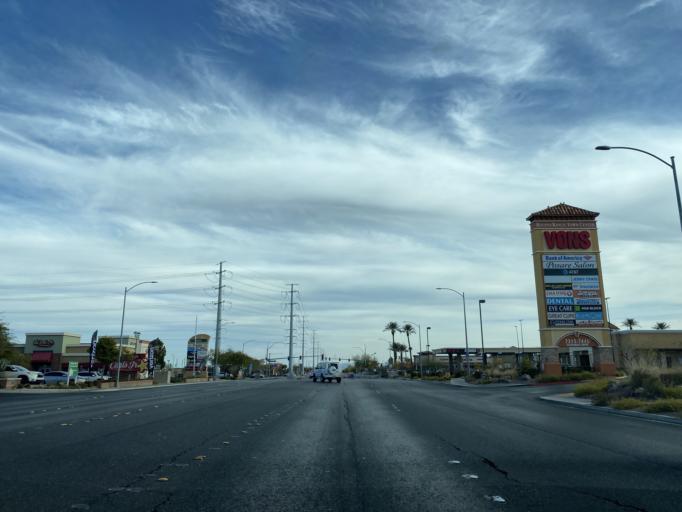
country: US
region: Nevada
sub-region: Clark County
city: Enterprise
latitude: 36.0555
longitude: -115.2815
